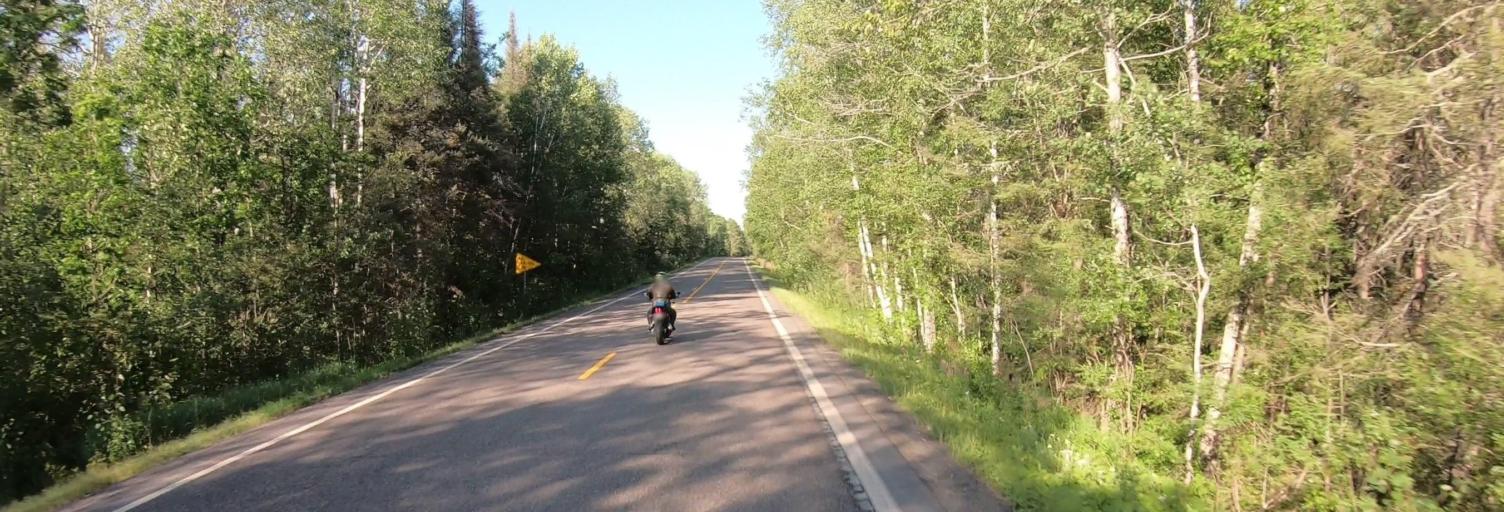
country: US
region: Minnesota
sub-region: Saint Louis County
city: Ely
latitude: 47.9385
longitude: -91.6790
